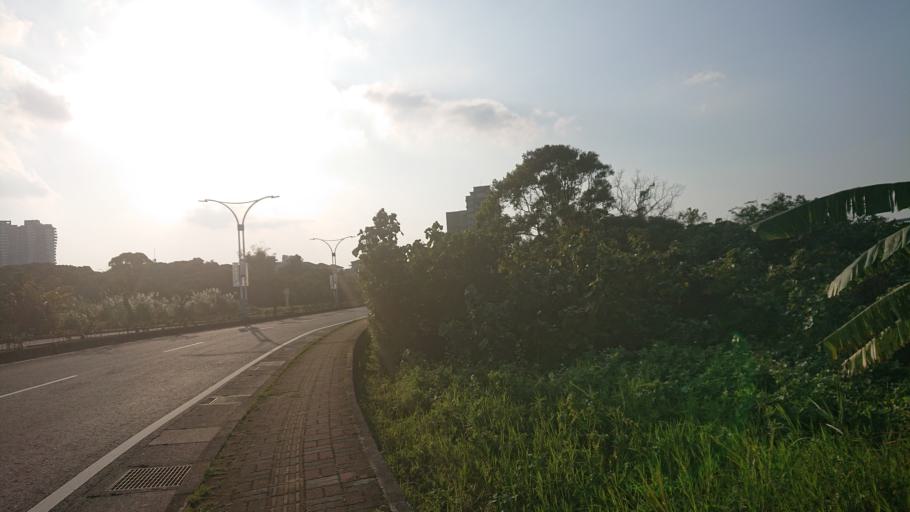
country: TW
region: Taipei
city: Taipei
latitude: 25.1884
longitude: 121.4256
